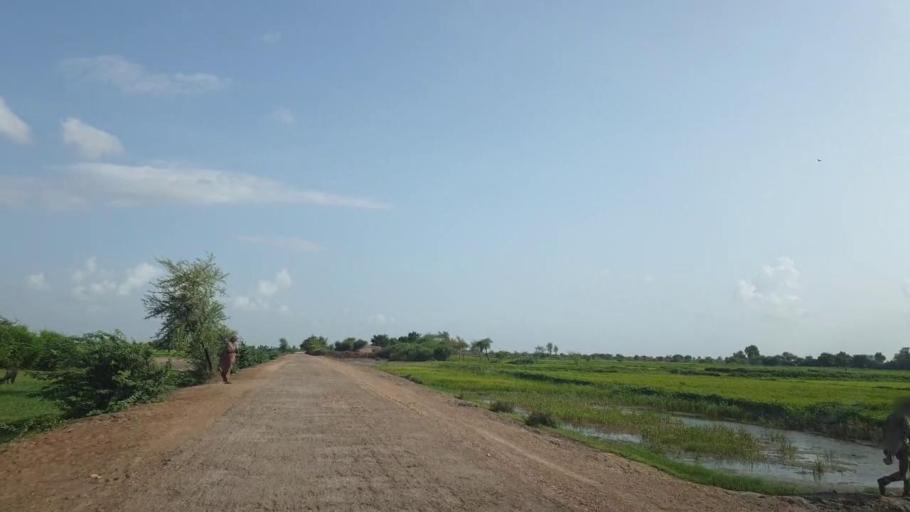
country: PK
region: Sindh
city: Kadhan
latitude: 24.6394
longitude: 69.0960
